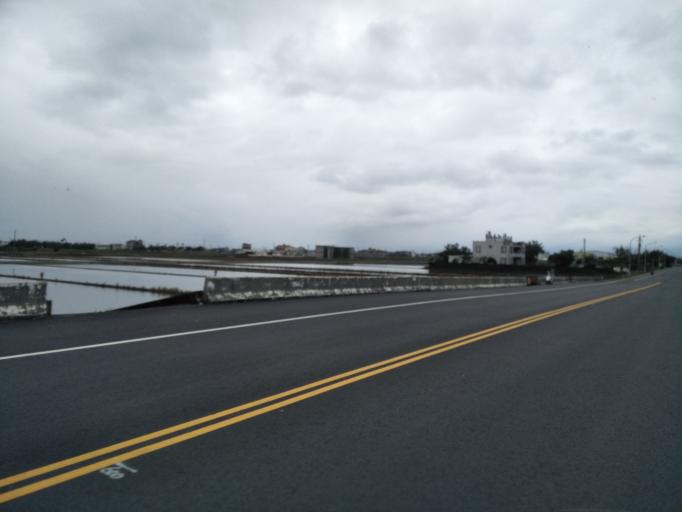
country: TW
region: Taiwan
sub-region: Yilan
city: Yilan
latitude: 24.8070
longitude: 121.7904
